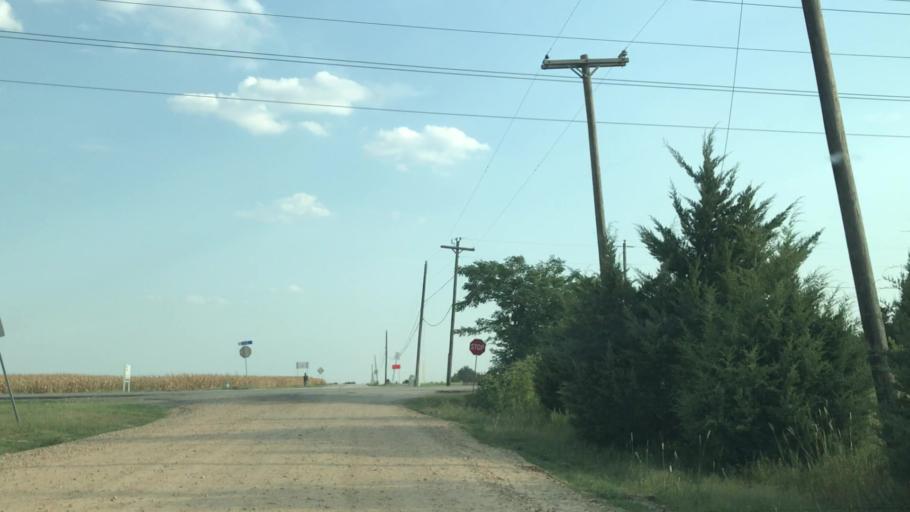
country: US
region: Texas
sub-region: Rockwall County
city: Fate
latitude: 32.9368
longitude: -96.4009
